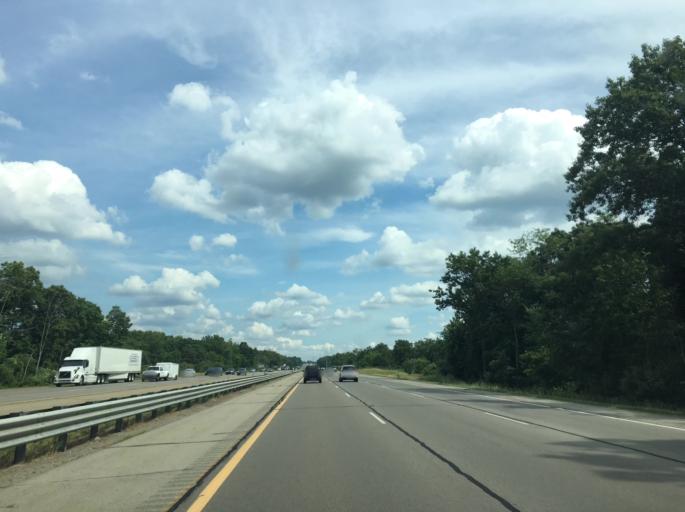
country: US
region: Michigan
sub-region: Oakland County
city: Holly
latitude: 42.8075
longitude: -83.5651
